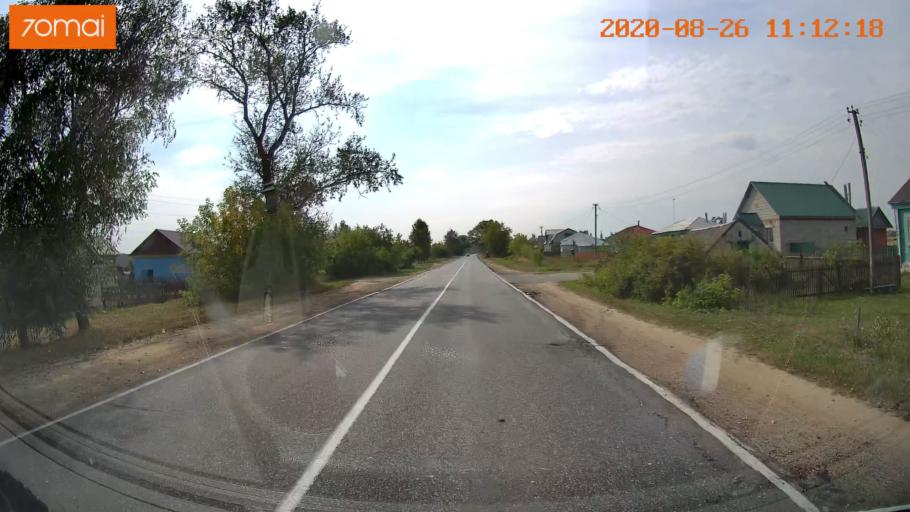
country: RU
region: Rjazan
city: Izhevskoye
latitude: 54.4718
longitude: 41.1253
